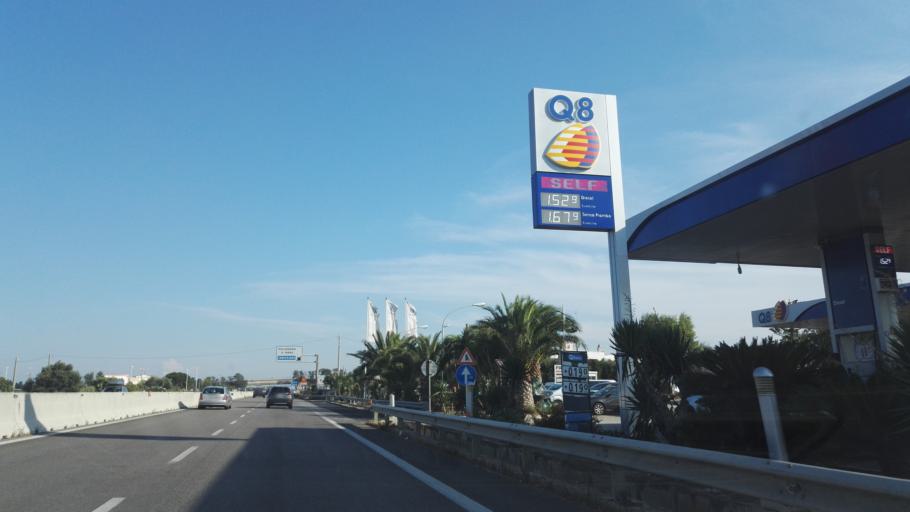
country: IT
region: Apulia
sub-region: Provincia di Bari
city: Polignano a Mare
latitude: 40.9948
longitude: 17.2045
